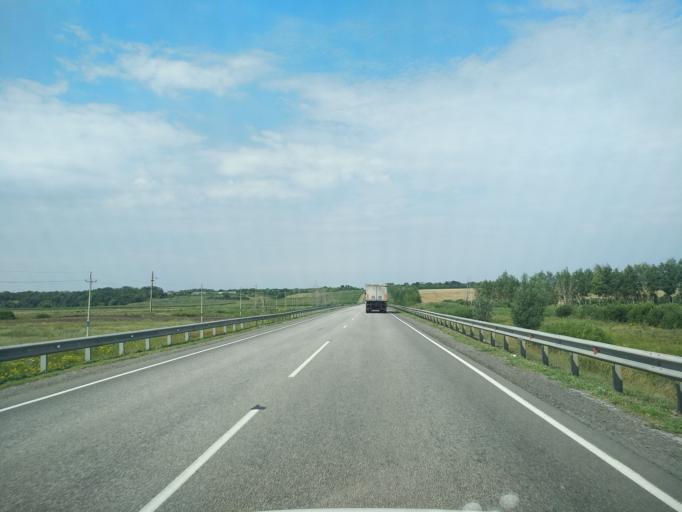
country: RU
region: Voronezj
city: Orlovo
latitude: 51.6758
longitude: 39.7333
